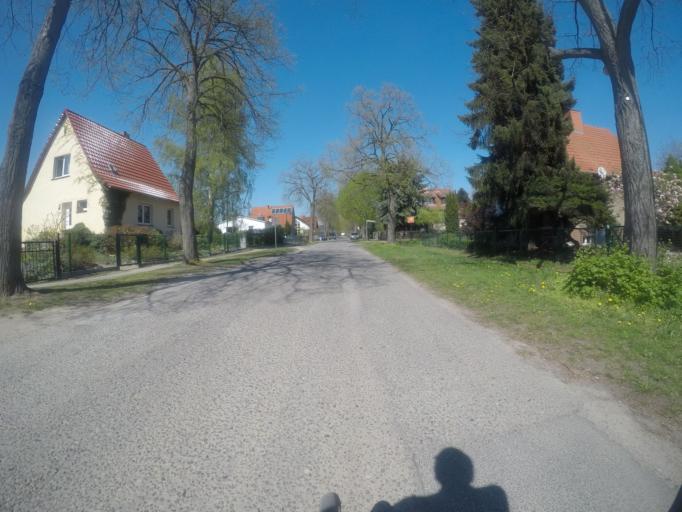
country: DE
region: Brandenburg
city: Bernau bei Berlin
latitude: 52.6836
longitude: 13.5898
